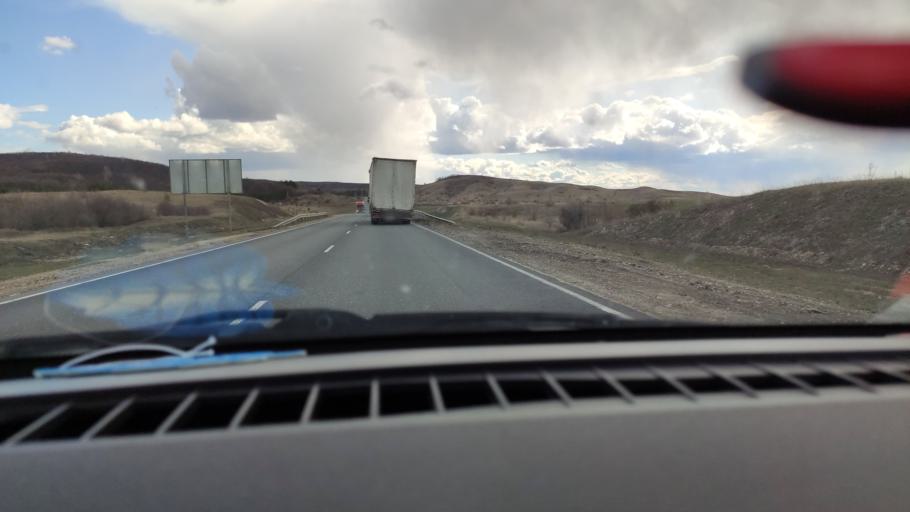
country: RU
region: Saratov
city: Alekseyevka
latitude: 52.3801
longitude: 47.9725
